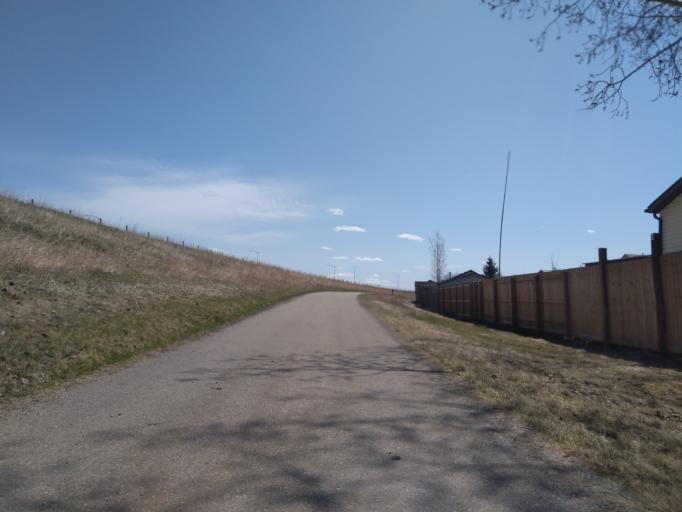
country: CA
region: Alberta
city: Chestermere
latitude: 51.0657
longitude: -113.9259
